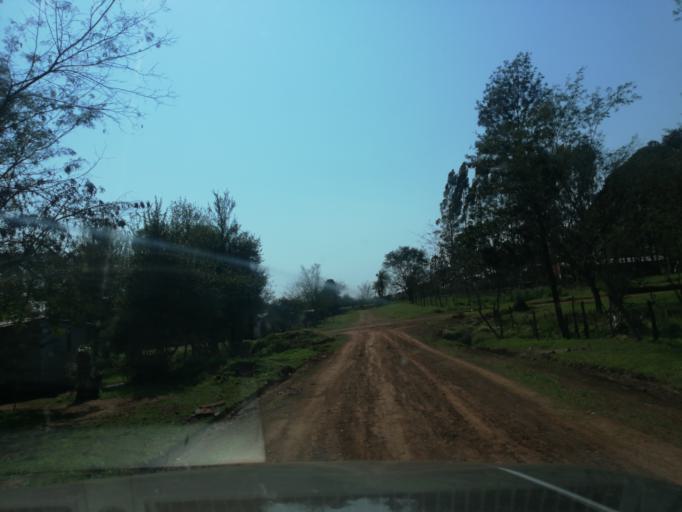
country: AR
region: Misiones
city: Bonpland
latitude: -27.4792
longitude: -55.4773
